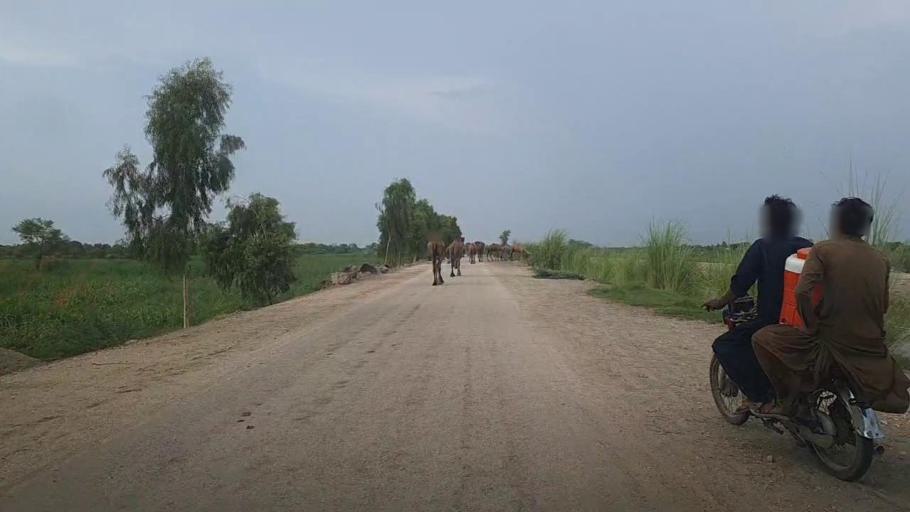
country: PK
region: Sindh
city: Karaundi
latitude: 26.9623
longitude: 68.4261
